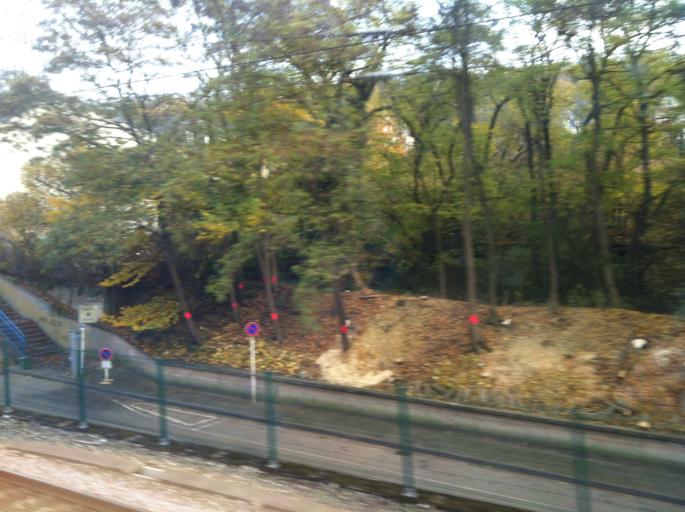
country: LU
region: Luxembourg
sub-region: Canton d'Esch-sur-Alzette
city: Esch-sur-Alzette
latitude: 49.4911
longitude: 5.9817
